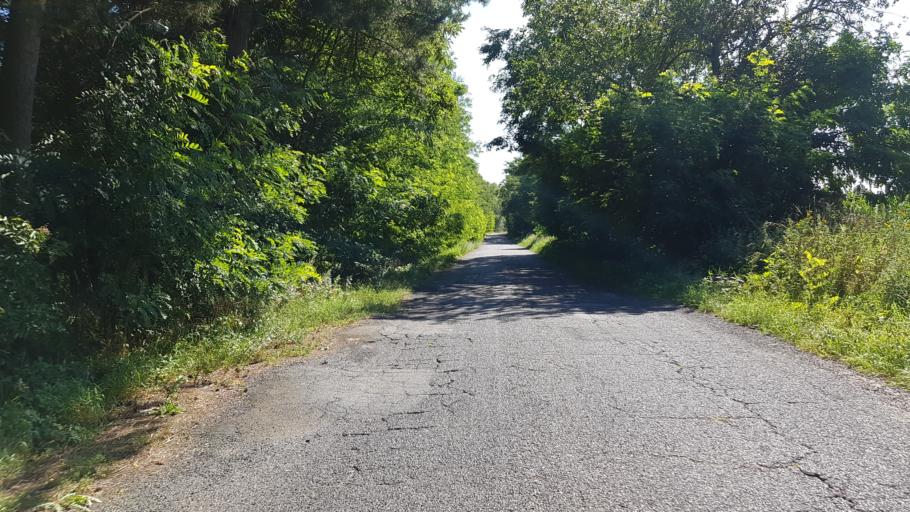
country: PL
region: West Pomeranian Voivodeship
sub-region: Powiat gryfinski
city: Gryfino
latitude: 53.1567
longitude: 14.5215
